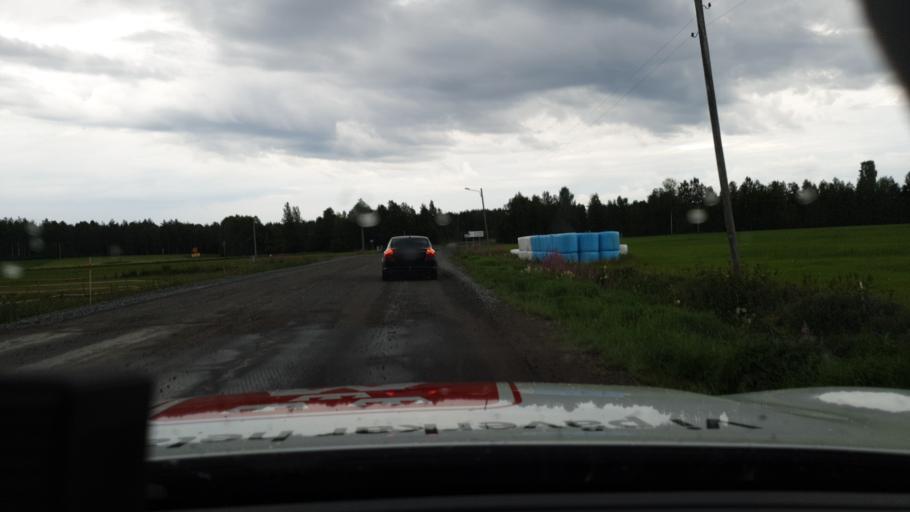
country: SE
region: Norrbotten
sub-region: Bodens Kommun
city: Boden
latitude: 65.8588
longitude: 21.4610
